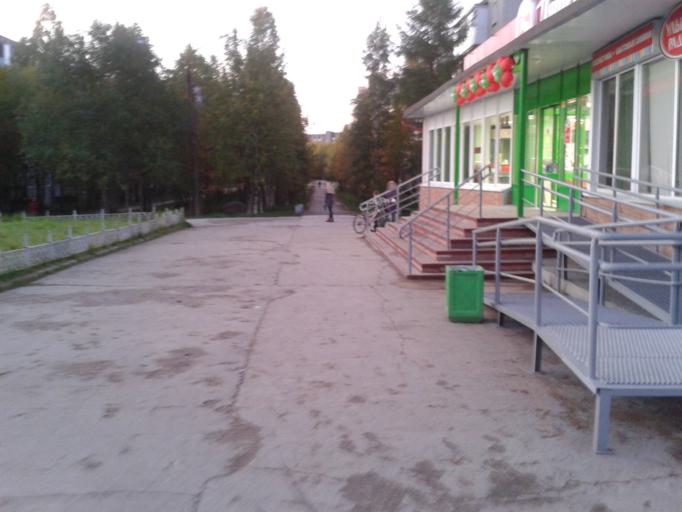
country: RU
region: Murmansk
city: Polyarnyye Zori
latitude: 67.3686
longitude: 32.4980
